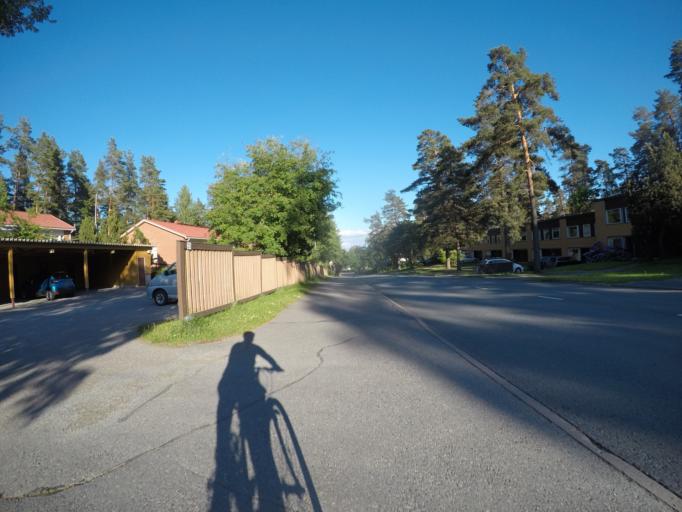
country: FI
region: Haeme
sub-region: Haemeenlinna
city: Haemeenlinna
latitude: 60.9809
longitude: 24.4575
